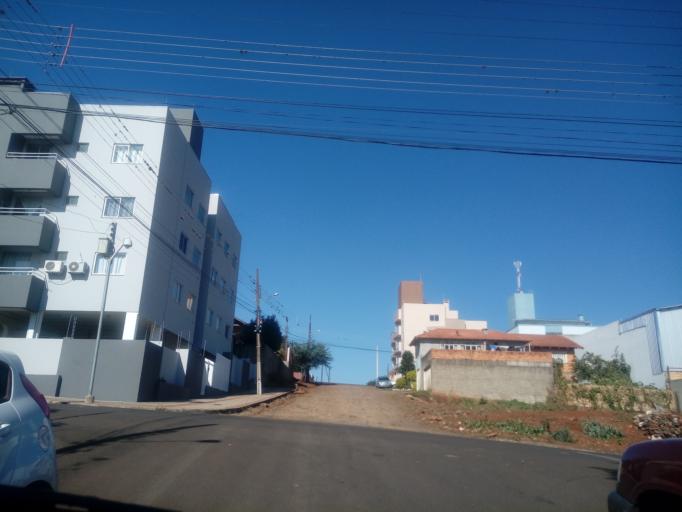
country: BR
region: Santa Catarina
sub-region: Chapeco
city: Chapeco
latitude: -27.0749
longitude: -52.6177
